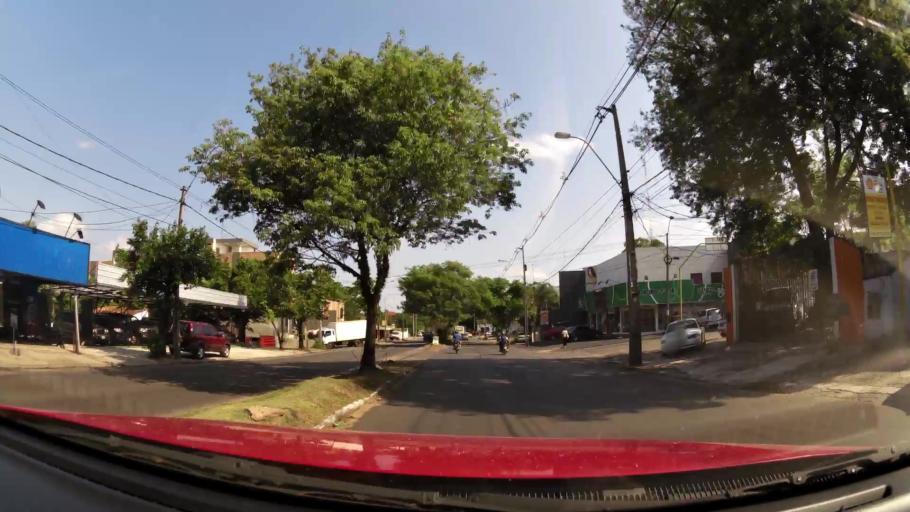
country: PY
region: Asuncion
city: Asuncion
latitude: -25.3062
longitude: -57.6320
